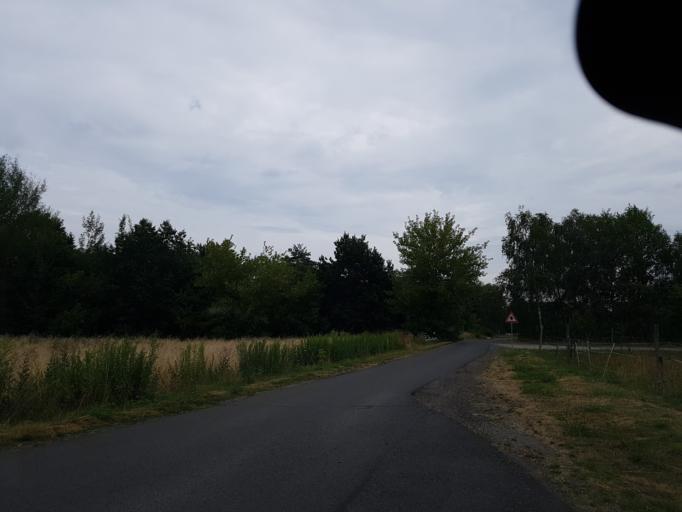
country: DE
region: Brandenburg
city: Schipkau
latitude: 51.5572
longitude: 13.8886
